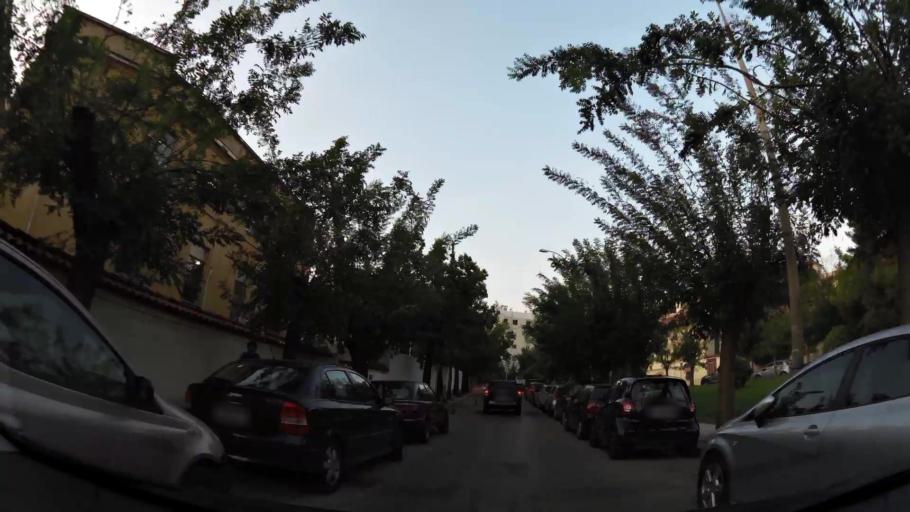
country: GR
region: Attica
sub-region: Nomarchia Athinas
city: Vyronas
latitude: 37.9846
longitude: 23.7548
